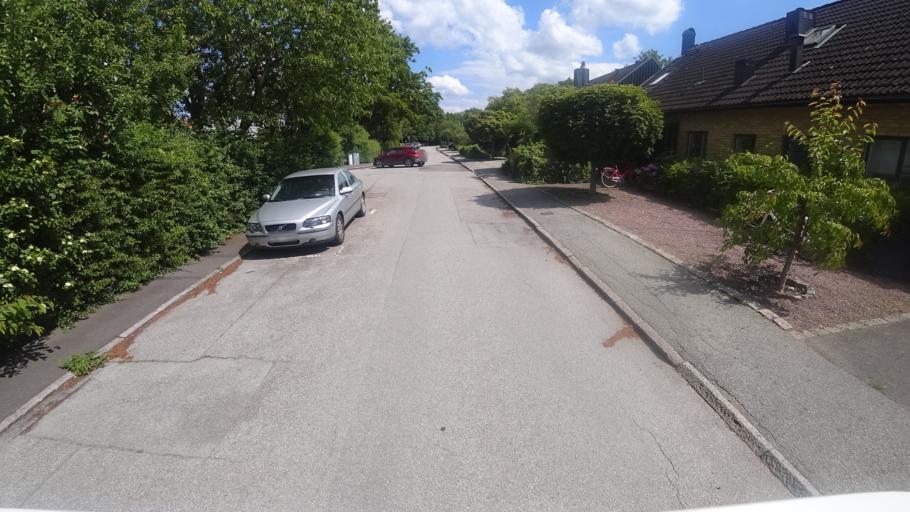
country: SE
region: Skane
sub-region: Lunds Kommun
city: Lund
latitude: 55.6957
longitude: 13.2074
